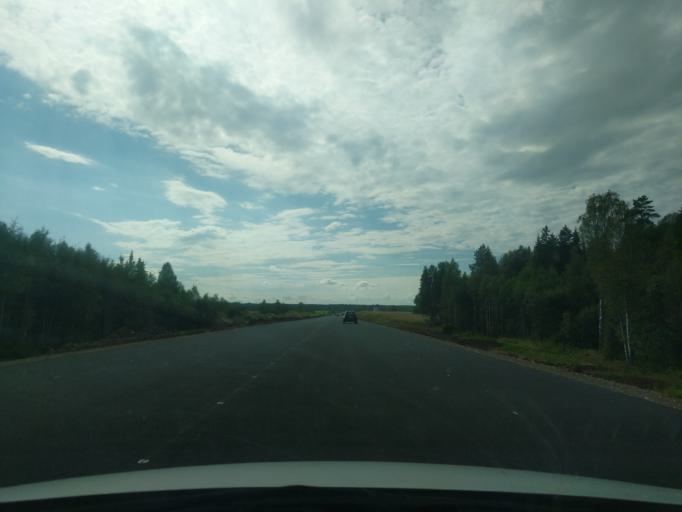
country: RU
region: Kostroma
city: Sudislavl'
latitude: 57.8141
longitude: 41.4747
